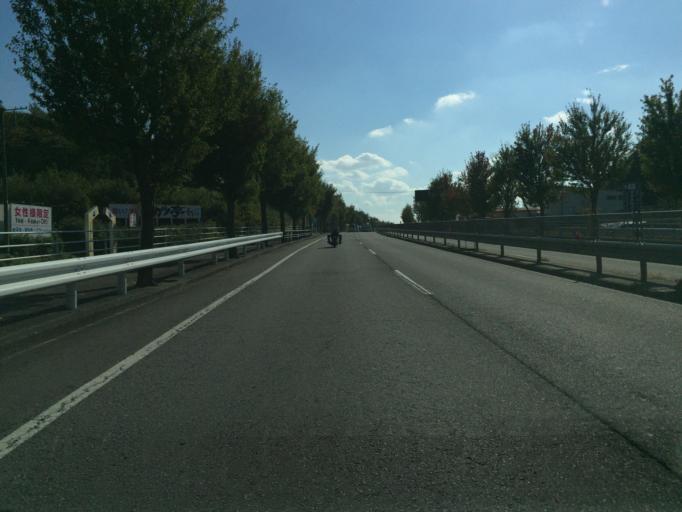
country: JP
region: Fukushima
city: Nihommatsu
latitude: 37.6445
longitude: 140.4866
